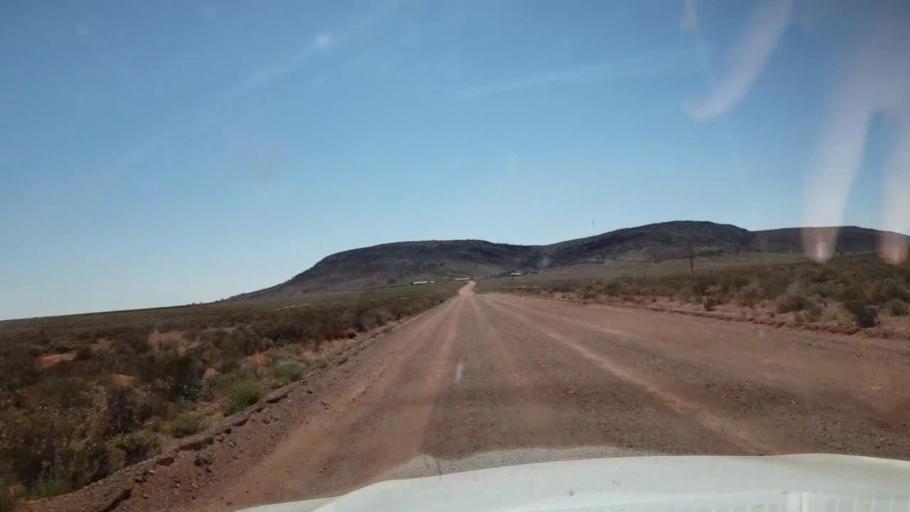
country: AU
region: South Australia
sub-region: Whyalla
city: Whyalla
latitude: -32.6962
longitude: 137.1317
